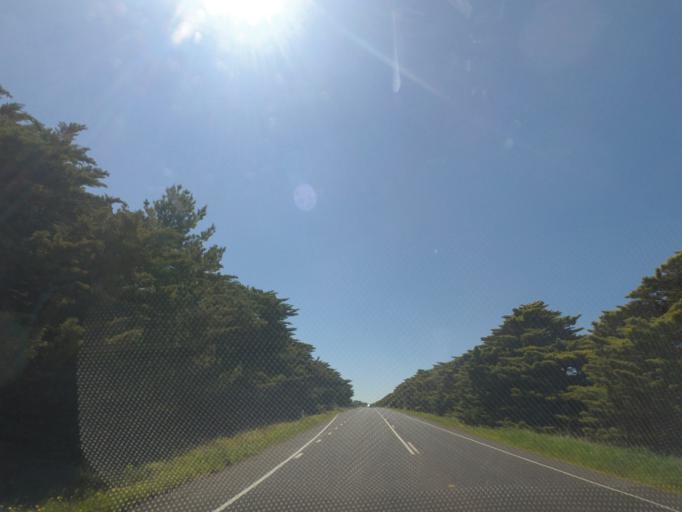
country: AU
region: Victoria
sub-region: Hume
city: Sunbury
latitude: -37.4351
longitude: 144.7462
